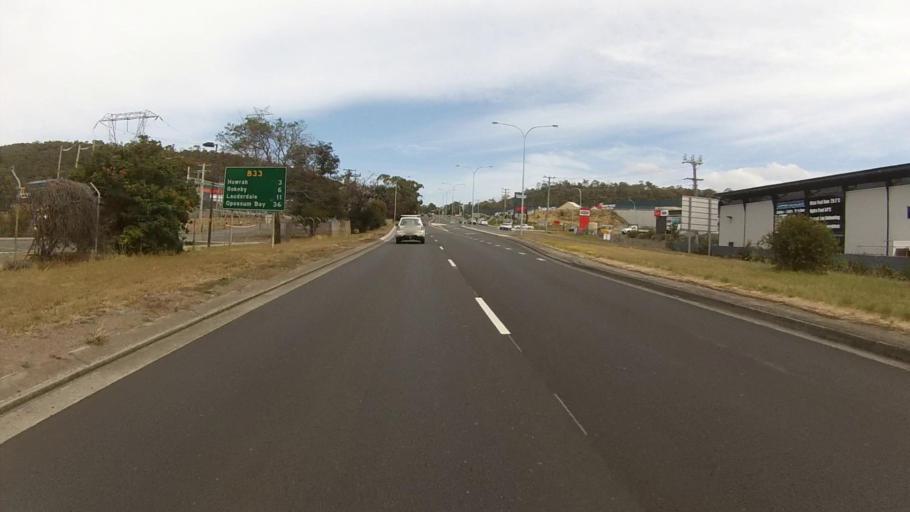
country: AU
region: Tasmania
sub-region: Clarence
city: Warrane
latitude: -42.8587
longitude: 147.3945
